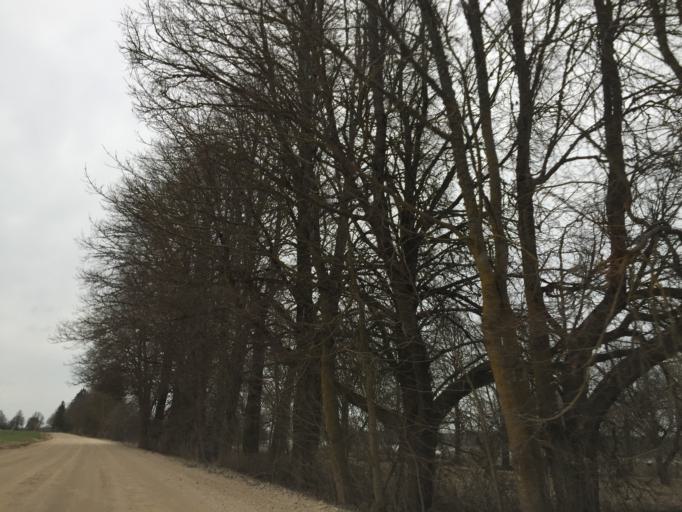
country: LV
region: Livani
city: Livani
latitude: 56.2904
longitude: 26.1761
